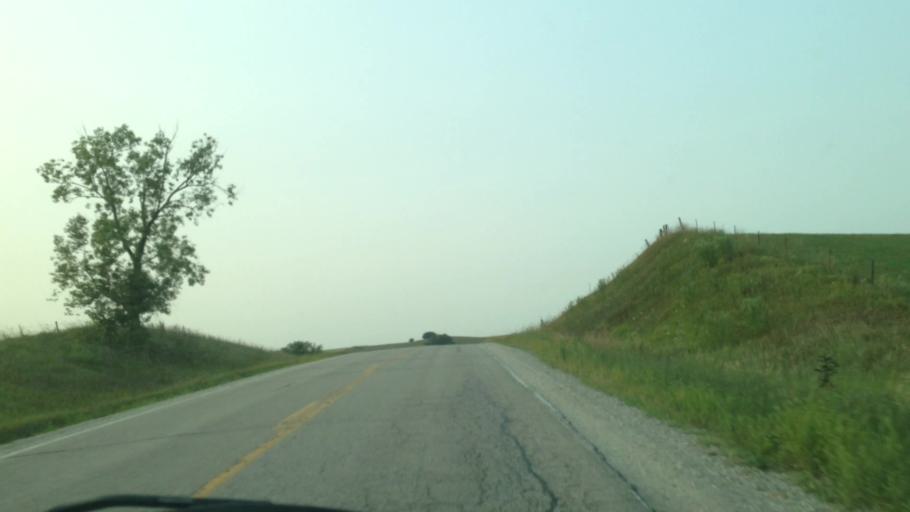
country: US
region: Iowa
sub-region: Iowa County
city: Marengo
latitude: 41.8788
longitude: -92.0890
